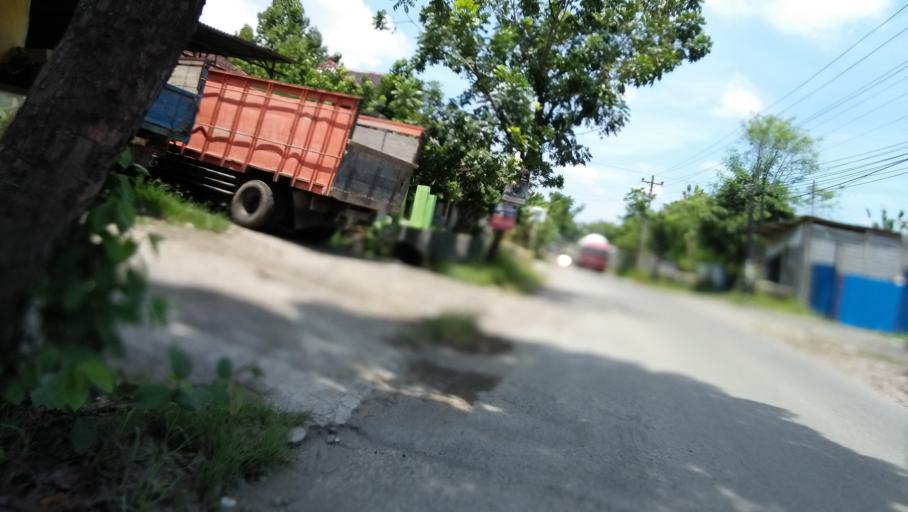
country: ID
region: Central Java
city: Mranggen
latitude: -7.0500
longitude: 110.4715
